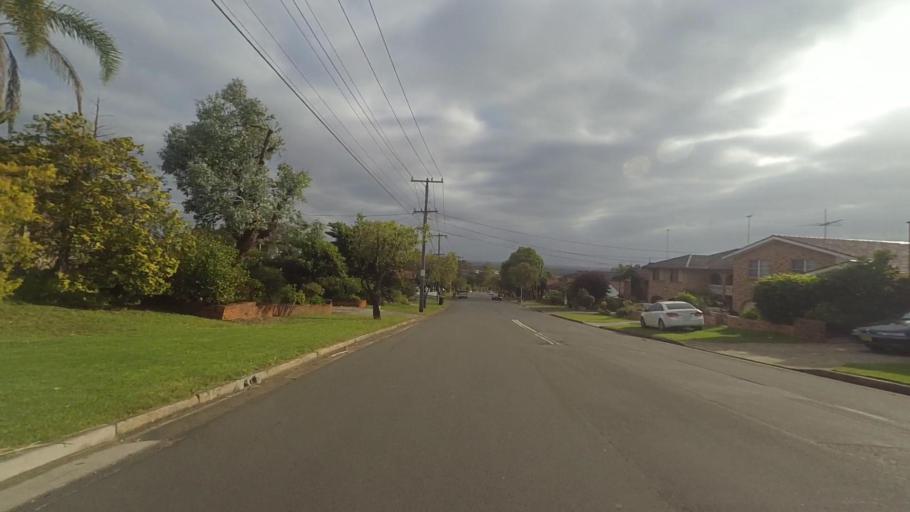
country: AU
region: New South Wales
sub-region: Bankstown
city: Regents Park
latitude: -33.9121
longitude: 151.0003
